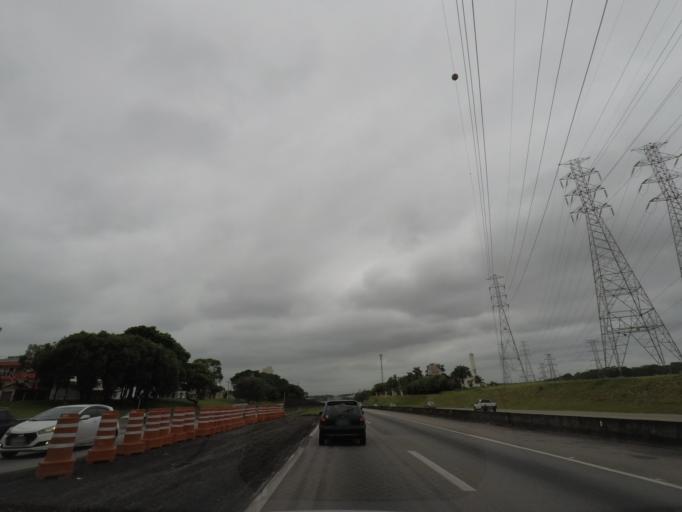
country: BR
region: Sao Paulo
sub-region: Sao Jose Dos Campos
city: Sao Jose dos Campos
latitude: -23.1854
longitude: -45.8516
